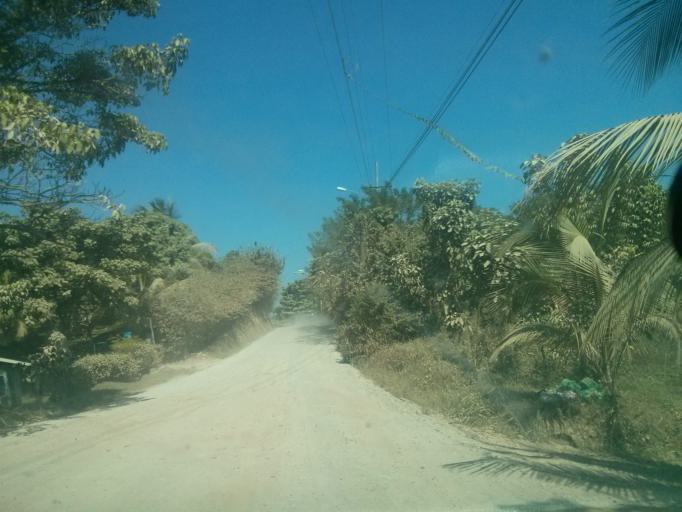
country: CR
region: Puntarenas
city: Paquera
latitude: 9.6613
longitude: -85.1198
